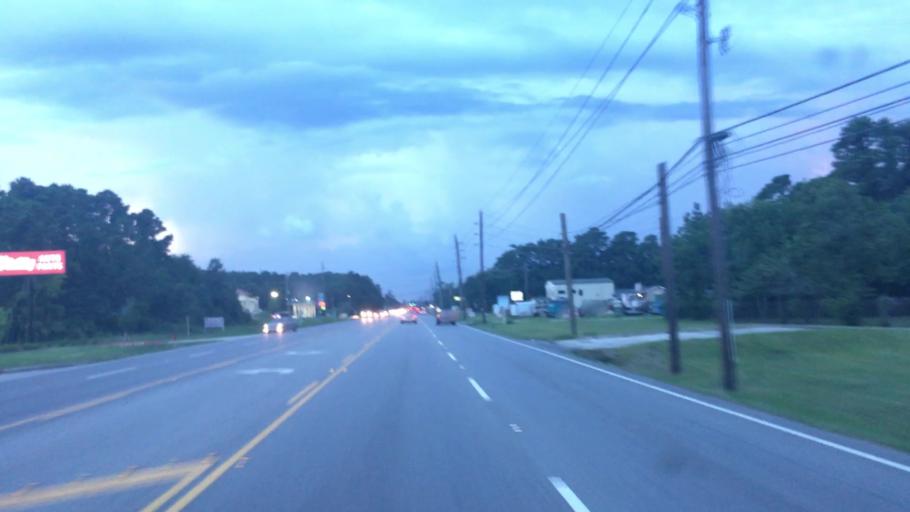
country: US
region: Texas
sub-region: Harris County
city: Atascocita
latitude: 29.9873
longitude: -95.1962
